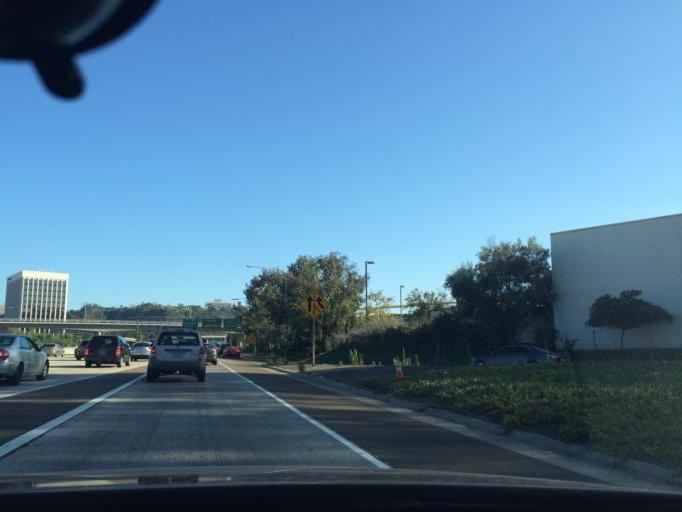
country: US
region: California
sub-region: San Diego County
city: San Diego
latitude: 32.7700
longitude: -117.1620
